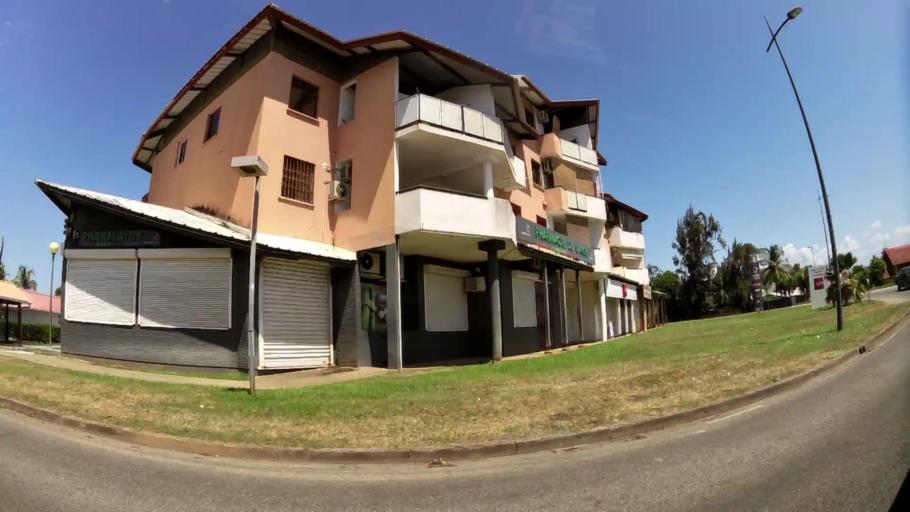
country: GF
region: Guyane
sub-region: Guyane
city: Kourou
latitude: 5.1727
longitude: -52.6497
